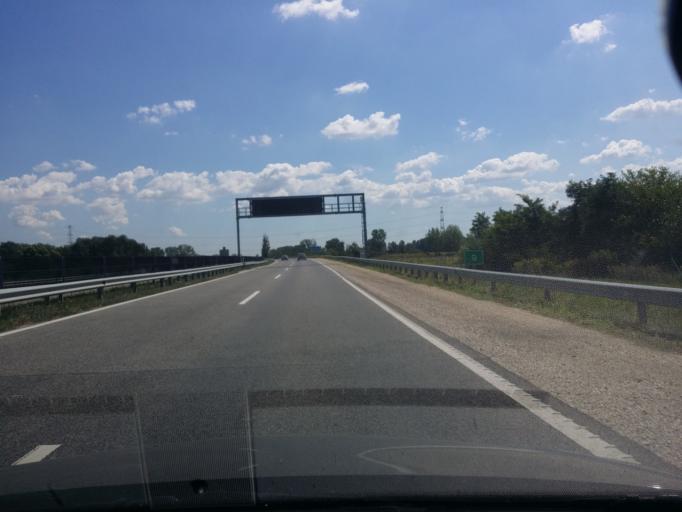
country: HU
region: Gyor-Moson-Sopron
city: Rabapatona
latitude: 47.6514
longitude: 17.4373
